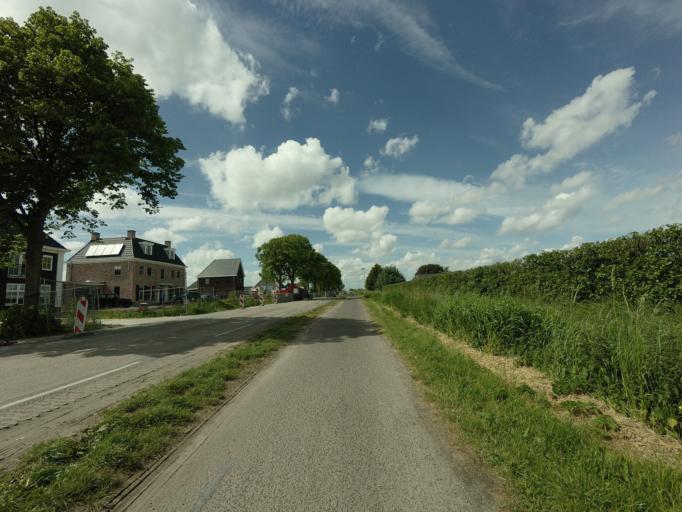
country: NL
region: North Holland
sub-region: Gemeente Hoorn
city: Hoorn
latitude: 52.6735
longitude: 5.0971
